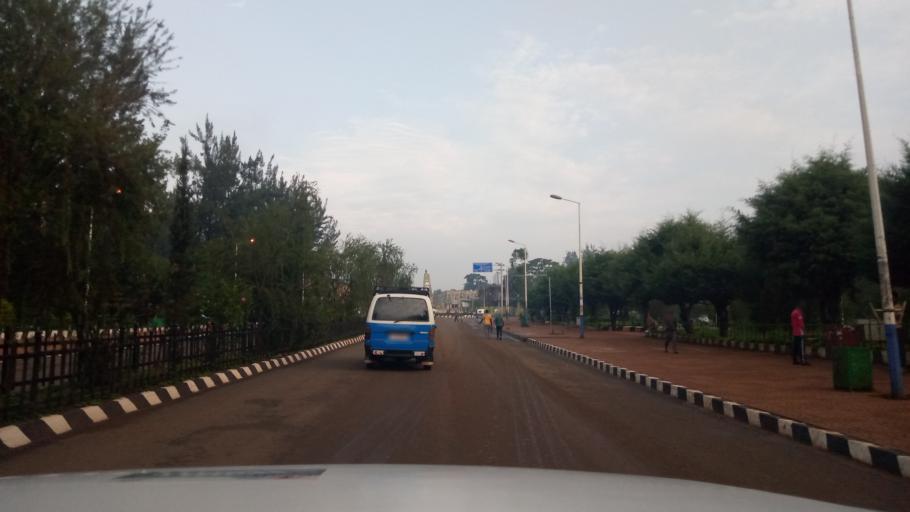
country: ET
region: Oromiya
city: Jima
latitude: 7.6759
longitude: 36.8359
